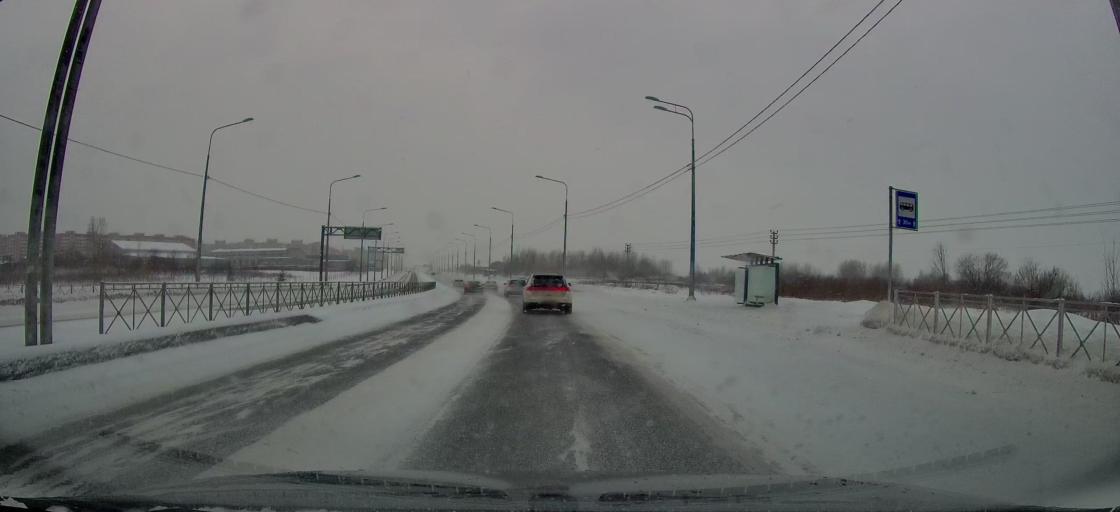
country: RU
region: St.-Petersburg
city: Krasnoye Selo
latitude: 59.7519
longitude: 30.0899
